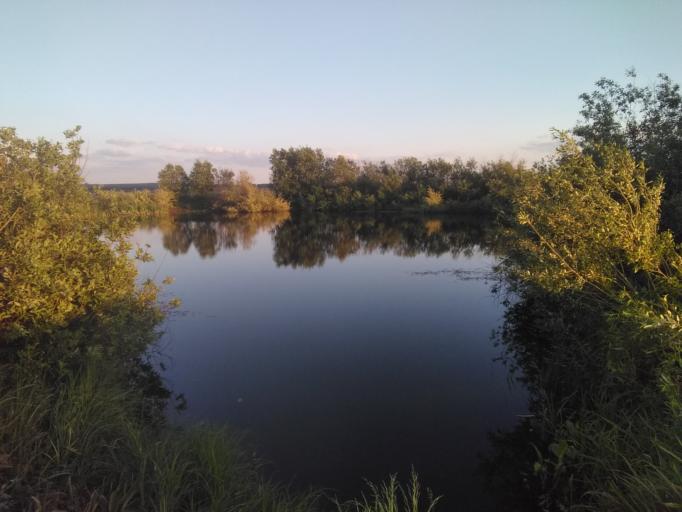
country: RU
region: Bashkortostan
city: Tolbazy
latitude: 53.9615
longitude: 55.9036
